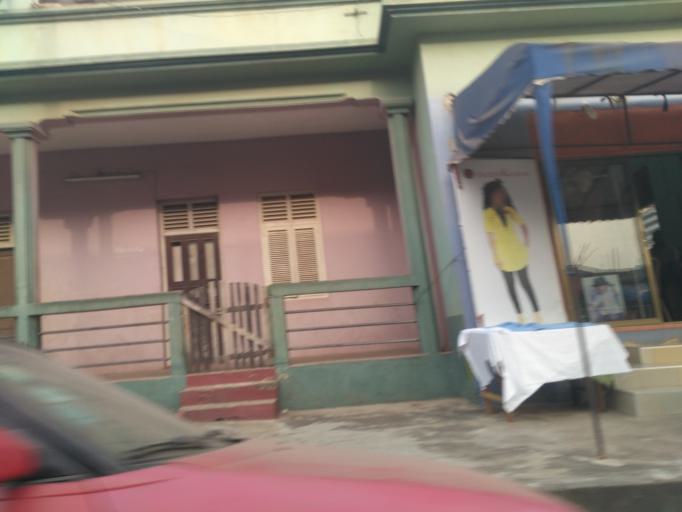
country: GH
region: Ashanti
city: Kumasi
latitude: 6.6853
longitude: -1.6128
